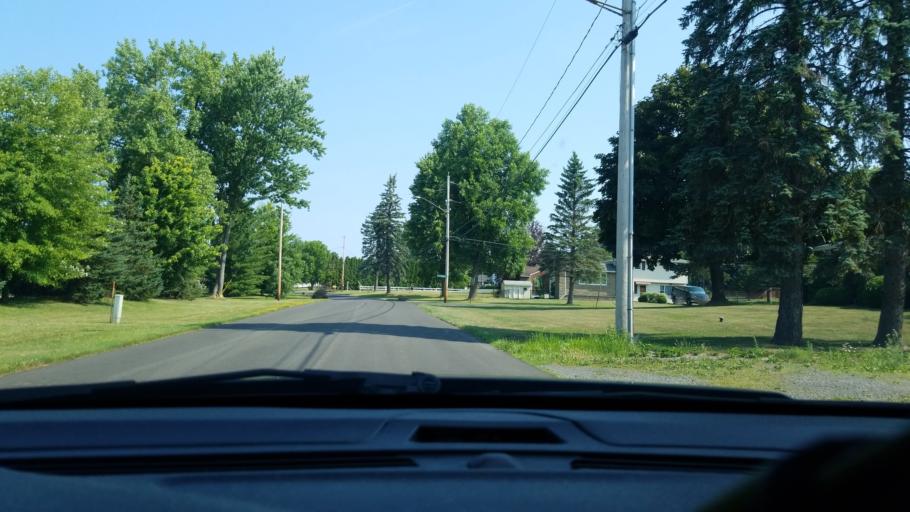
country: US
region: New York
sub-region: Onondaga County
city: East Syracuse
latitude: 43.0992
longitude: -76.0713
